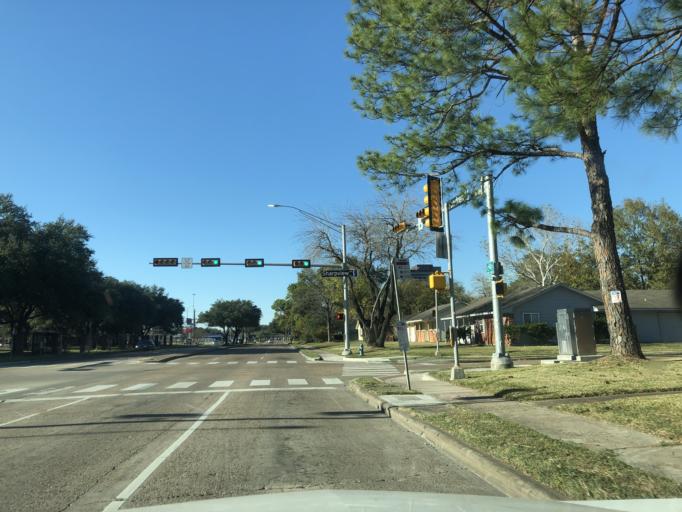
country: US
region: Texas
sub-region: Harris County
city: Bellaire
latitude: 29.6969
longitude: -95.5137
